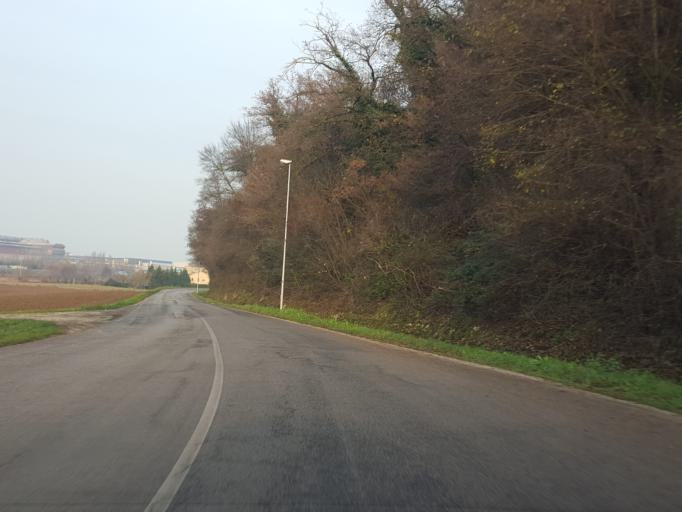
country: IT
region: Veneto
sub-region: Provincia di Vicenza
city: Altavilla Vicentina
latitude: 45.5096
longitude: 11.4912
